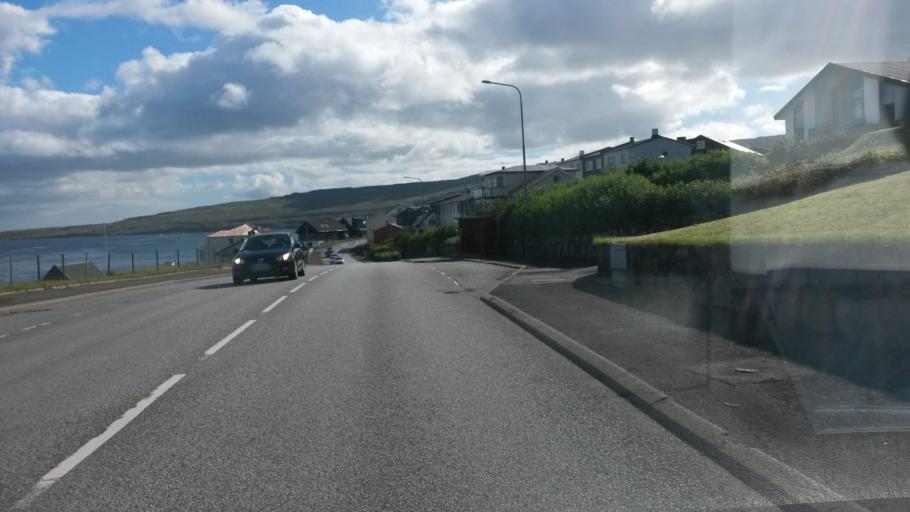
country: FO
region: Streymoy
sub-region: Torshavn
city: Torshavn
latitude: 62.0119
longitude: -6.7591
